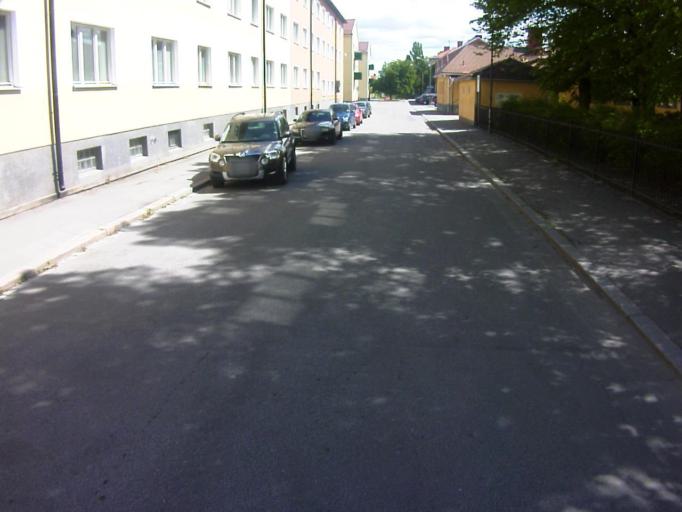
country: SE
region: Soedermanland
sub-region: Eskilstuna Kommun
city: Eskilstuna
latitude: 59.3655
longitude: 16.5067
